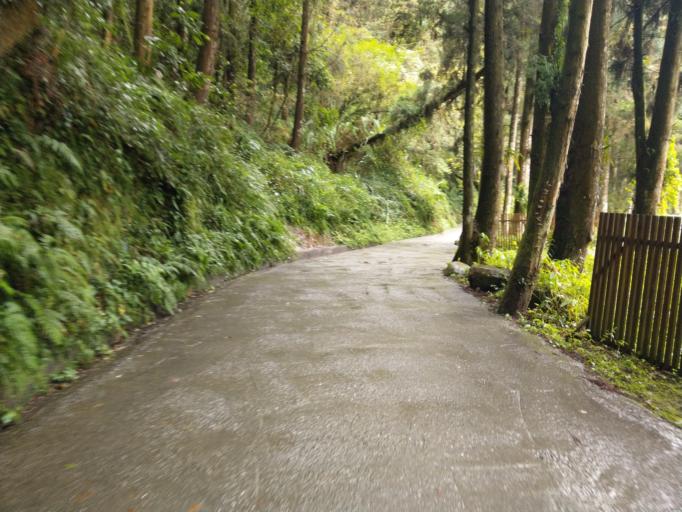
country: TW
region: Taiwan
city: Lugu
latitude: 23.6383
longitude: 120.7898
